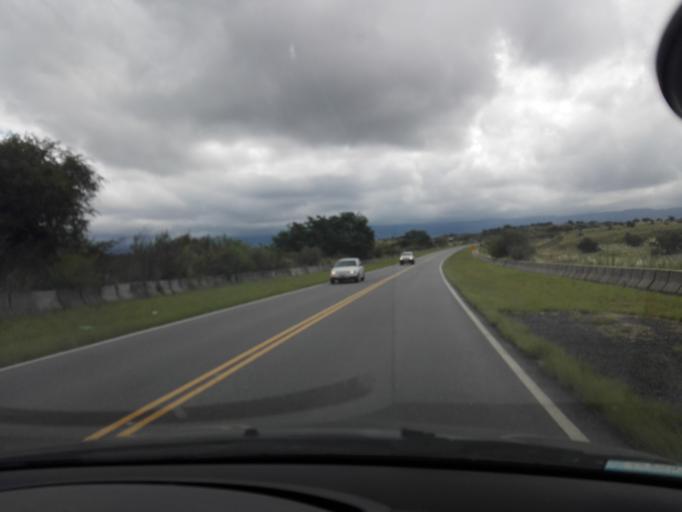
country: AR
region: Cordoba
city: Cuesta Blanca
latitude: -31.5754
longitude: -64.5952
